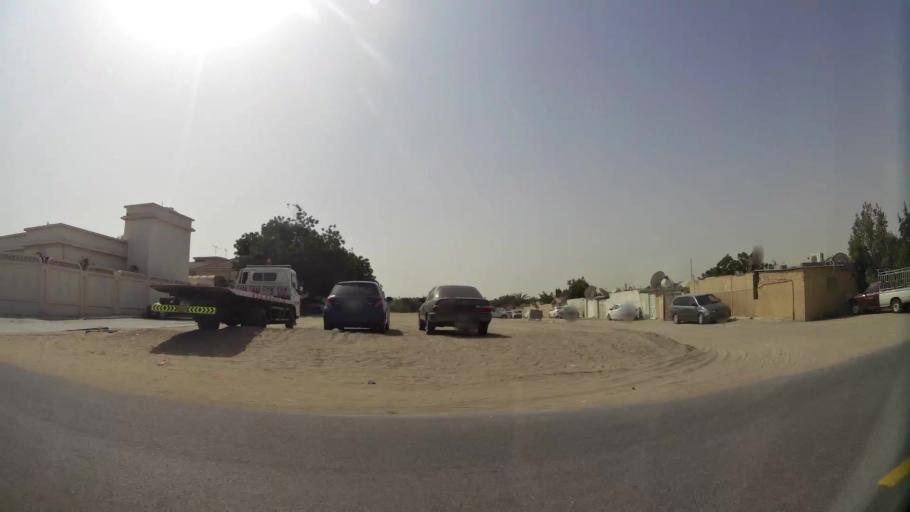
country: AE
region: Ash Shariqah
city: Sharjah
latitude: 25.3452
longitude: 55.4128
